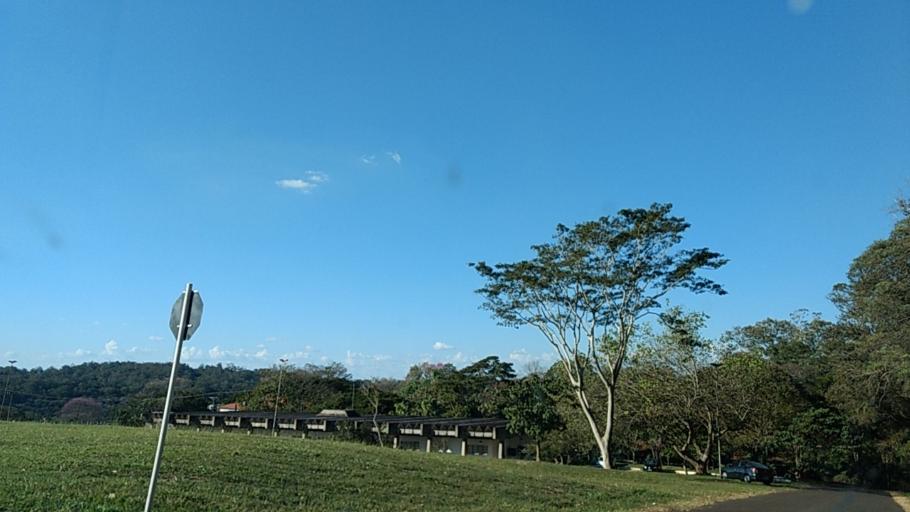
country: BR
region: Sao Paulo
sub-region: Botucatu
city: Botucatu
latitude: -22.8487
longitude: -48.4321
